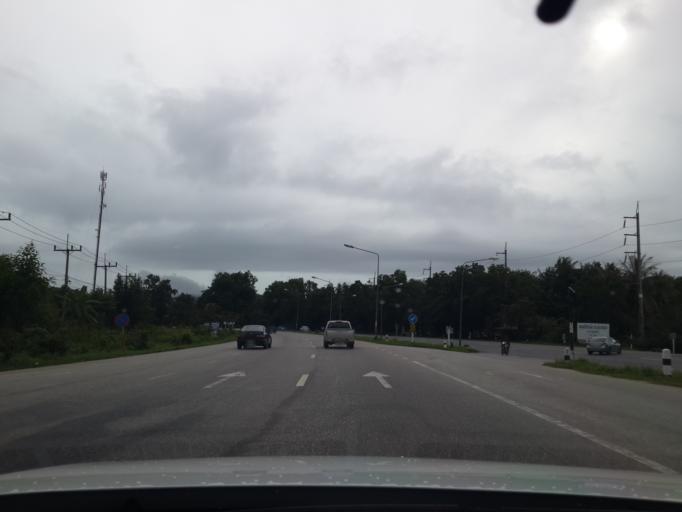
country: TH
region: Songkhla
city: Na Mom
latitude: 6.9551
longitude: 100.5577
